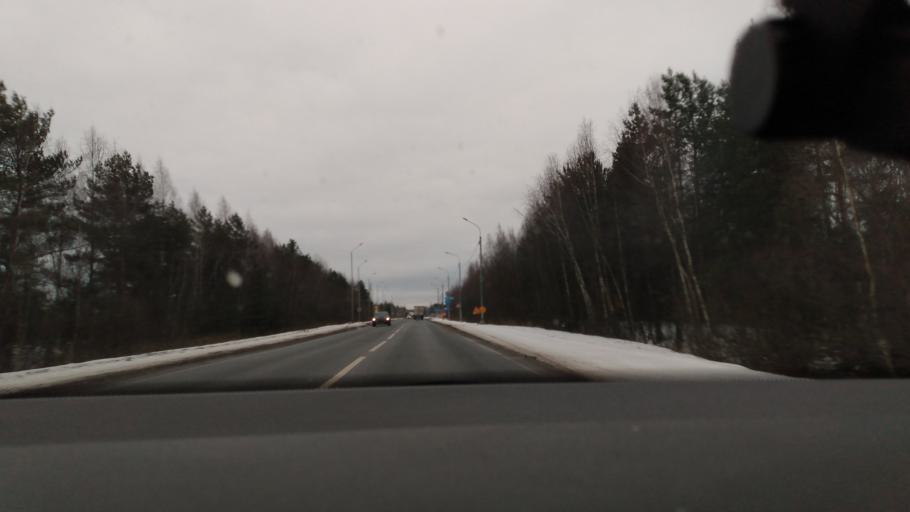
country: RU
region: Moskovskaya
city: Yegor'yevsk
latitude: 55.4207
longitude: 39.0404
